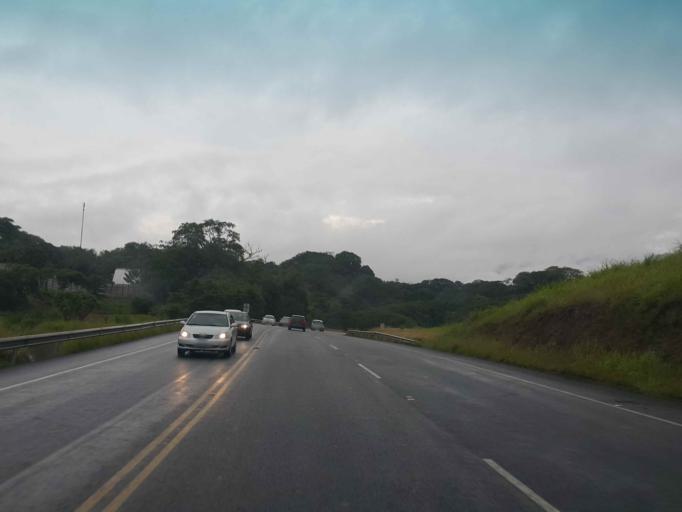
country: CR
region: Heredia
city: Colon
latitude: 9.9423
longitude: -84.2275
